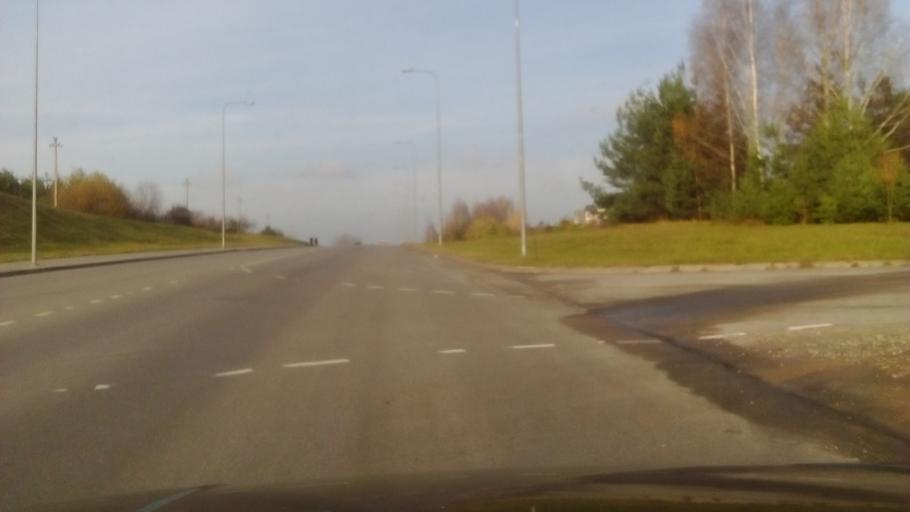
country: LT
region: Alytaus apskritis
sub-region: Alytus
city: Alytus
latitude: 54.3937
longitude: 23.9988
